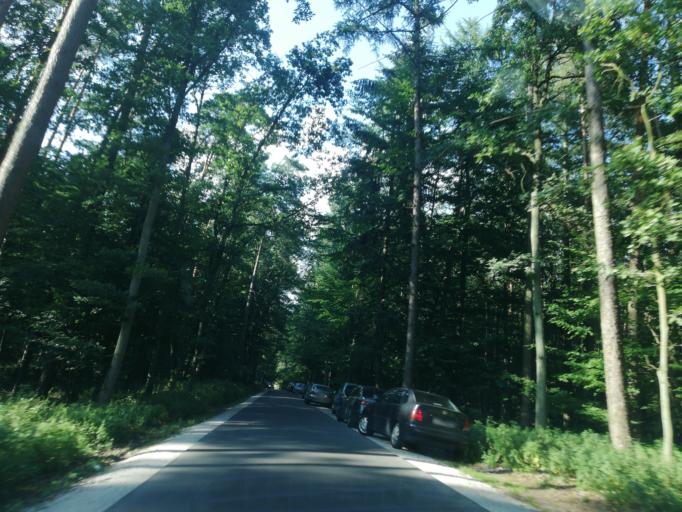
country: PL
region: Kujawsko-Pomorskie
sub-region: Powiat golubsko-dobrzynski
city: Ciechocin
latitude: 53.0781
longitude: 18.9500
